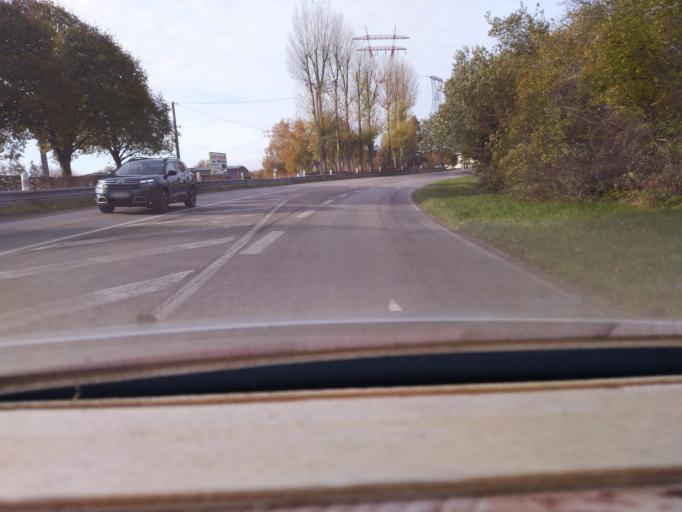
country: FR
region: Haute-Normandie
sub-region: Departement de la Seine-Maritime
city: Yainville
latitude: 49.4586
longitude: 0.8259
